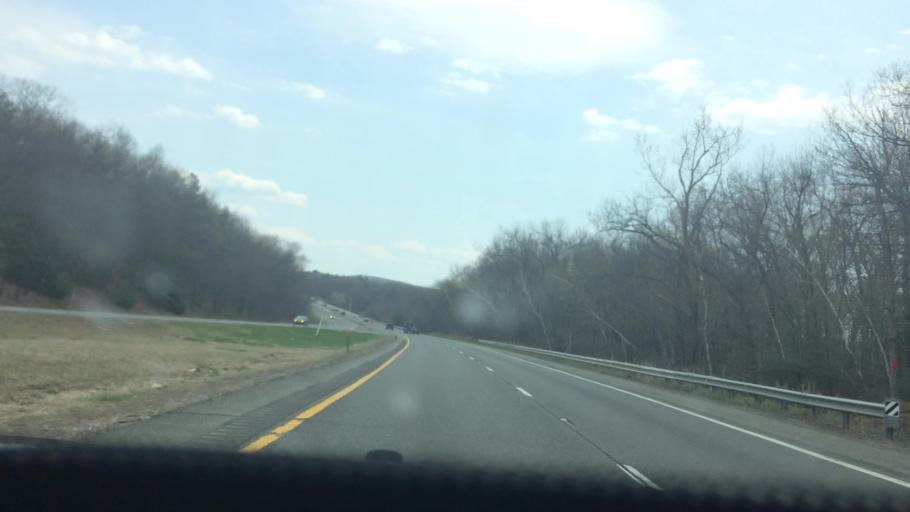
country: US
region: Massachusetts
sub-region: Hampden County
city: Wilbraham
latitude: 42.1587
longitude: -72.4161
